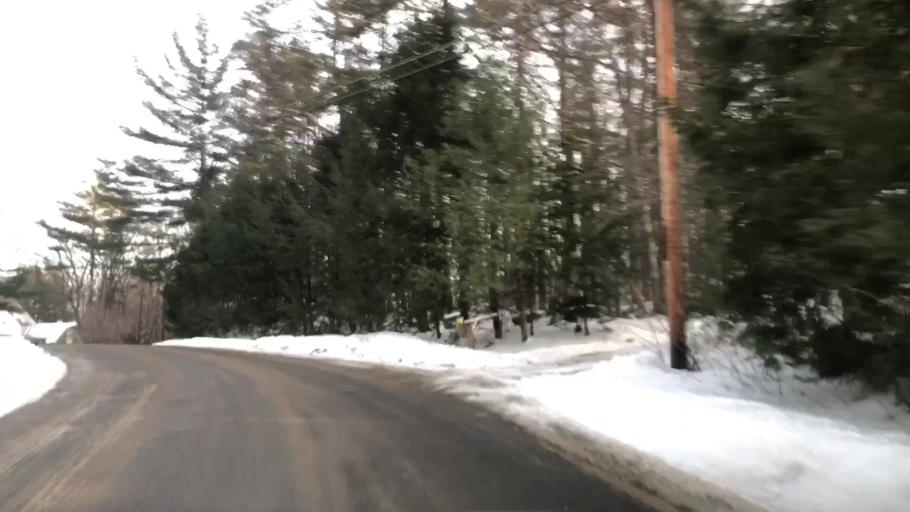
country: US
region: New Hampshire
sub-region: Hillsborough County
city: Wilton
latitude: 42.8273
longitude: -71.7014
